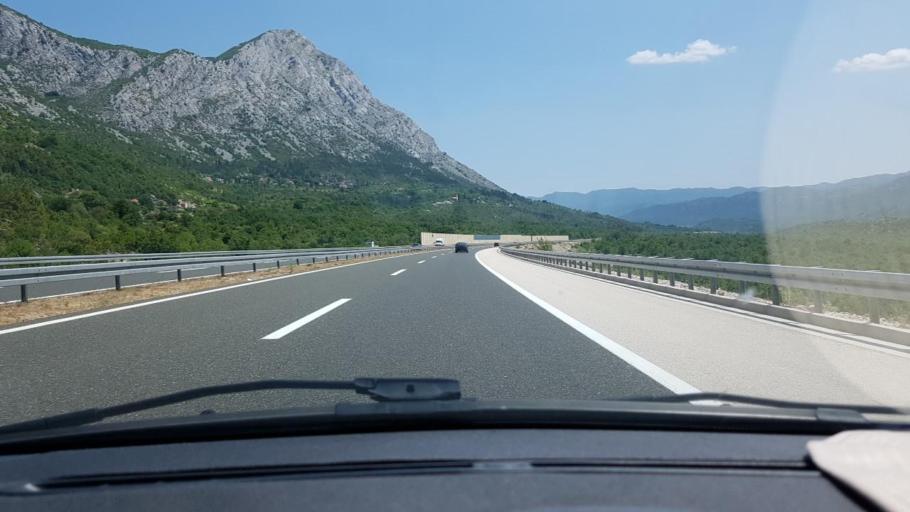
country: HR
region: Splitsko-Dalmatinska
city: Runovic
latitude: 43.2819
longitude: 17.2092
